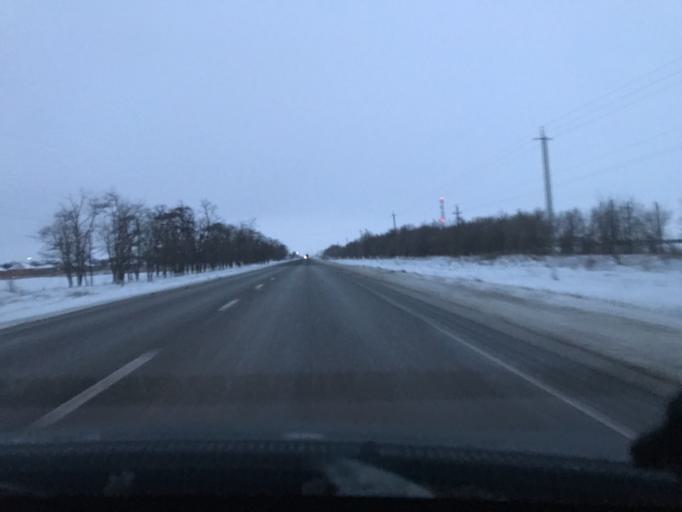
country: RU
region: Rostov
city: Letnik
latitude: 45.9109
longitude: 41.2933
